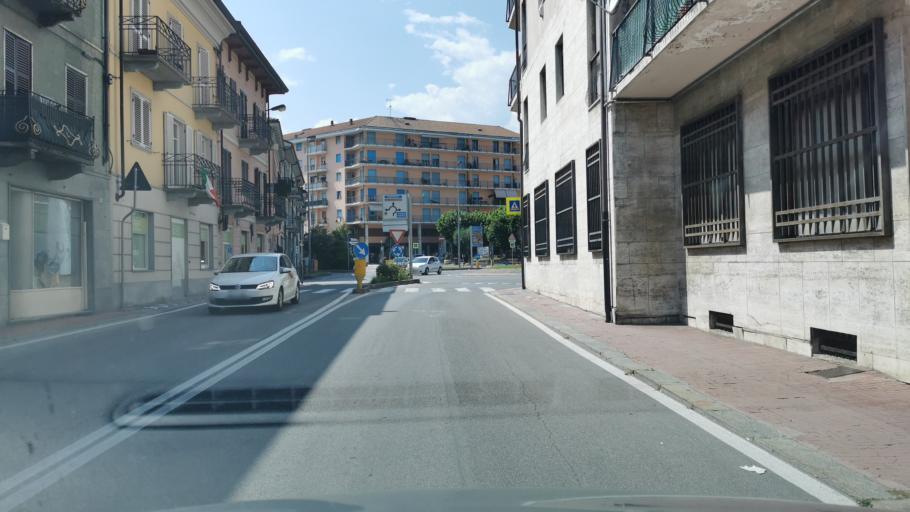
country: IT
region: Piedmont
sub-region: Provincia di Cuneo
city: Borgo San Dalmazzo
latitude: 44.3317
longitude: 7.4895
